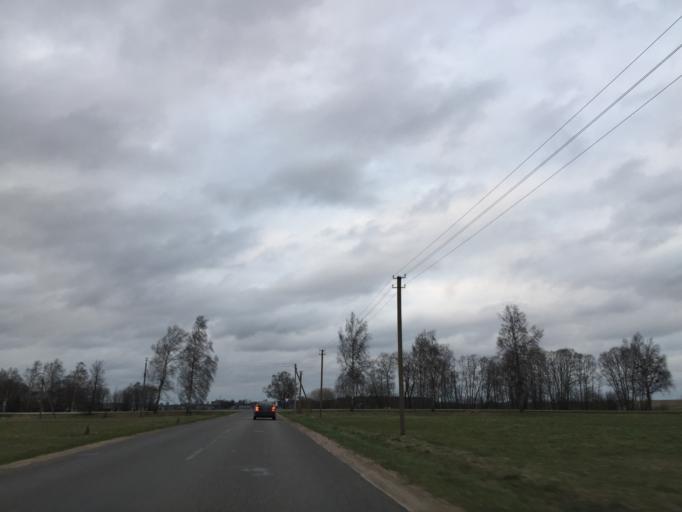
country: LT
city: Skaudvile
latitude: 55.4909
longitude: 22.5893
